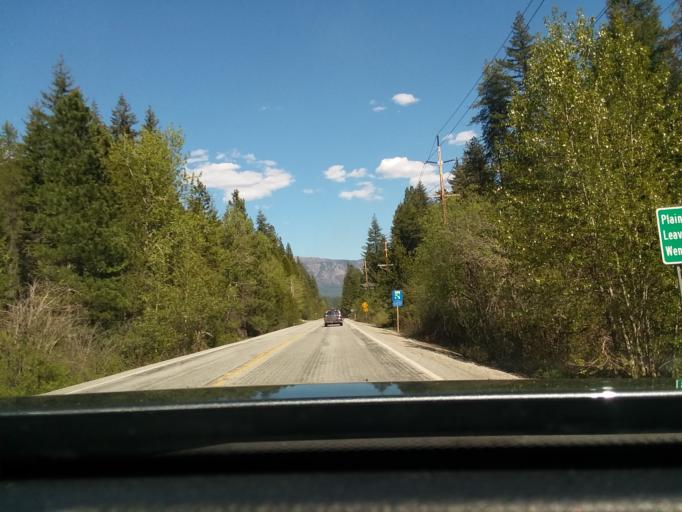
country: US
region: Washington
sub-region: Chelan County
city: Leavenworth
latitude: 47.8036
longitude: -120.7118
